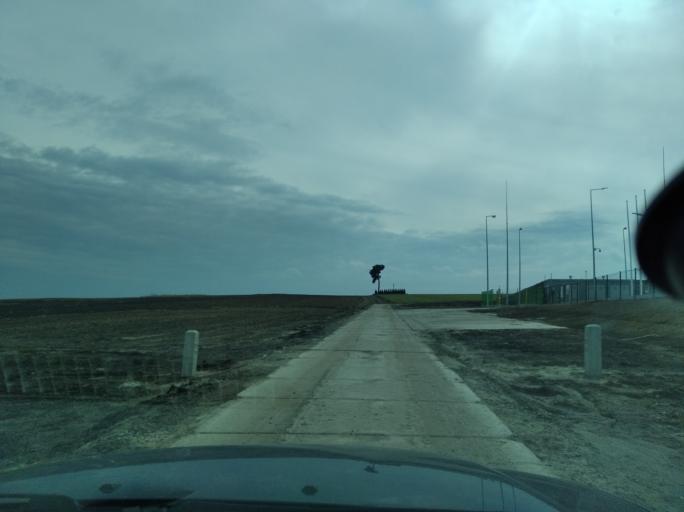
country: PL
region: Subcarpathian Voivodeship
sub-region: Powiat jaroslawski
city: Rokietnica
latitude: 49.9256
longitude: 22.5962
